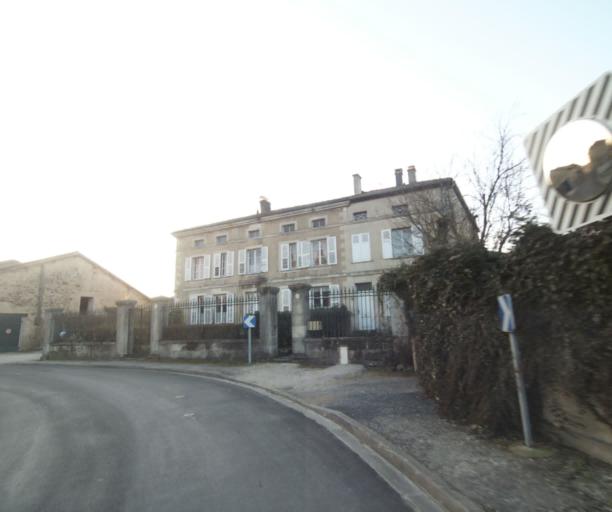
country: FR
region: Champagne-Ardenne
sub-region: Departement de la Haute-Marne
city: Bienville
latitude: 48.6065
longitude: 5.0383
